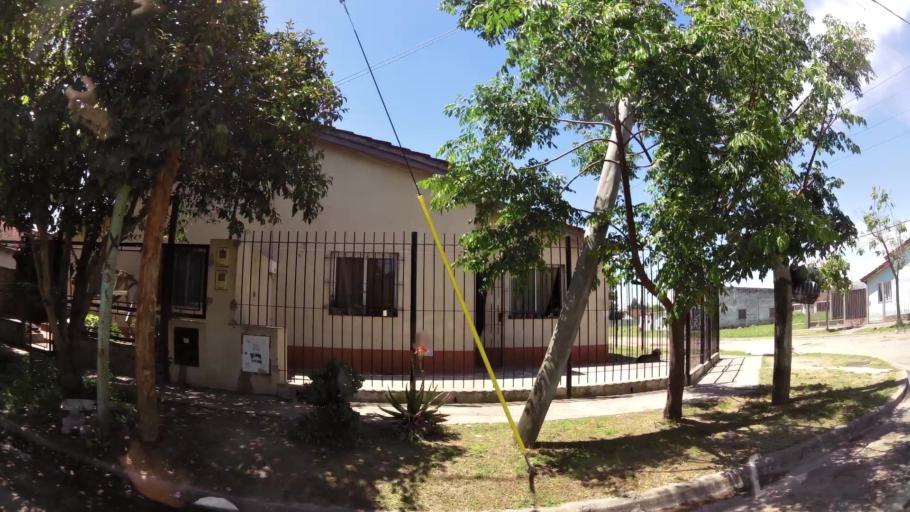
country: AR
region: Buenos Aires
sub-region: Partido de Quilmes
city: Quilmes
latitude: -34.7474
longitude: -58.3090
